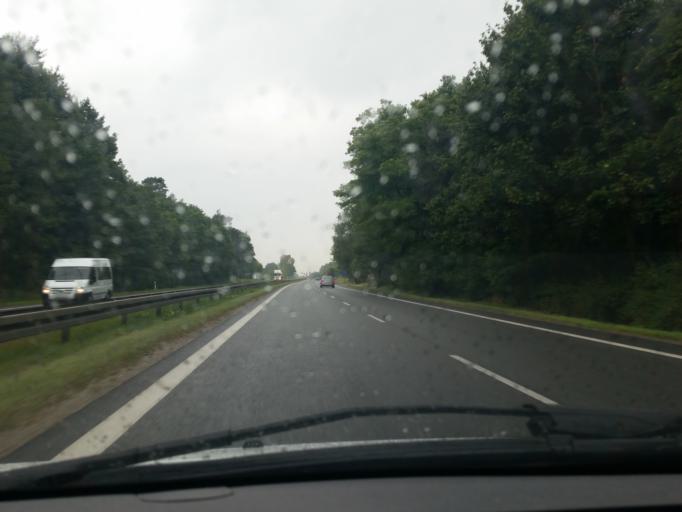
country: PL
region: Lodz Voivodeship
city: Zabia Wola
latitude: 52.0578
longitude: 20.7314
